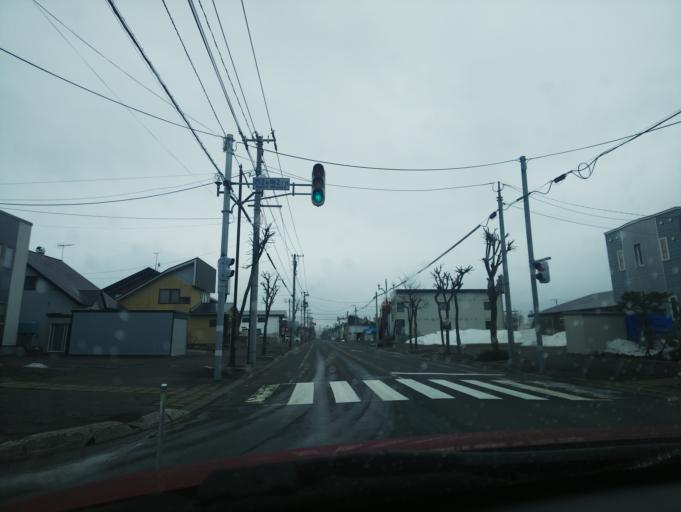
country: JP
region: Hokkaido
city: Nayoro
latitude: 44.3551
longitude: 142.4605
